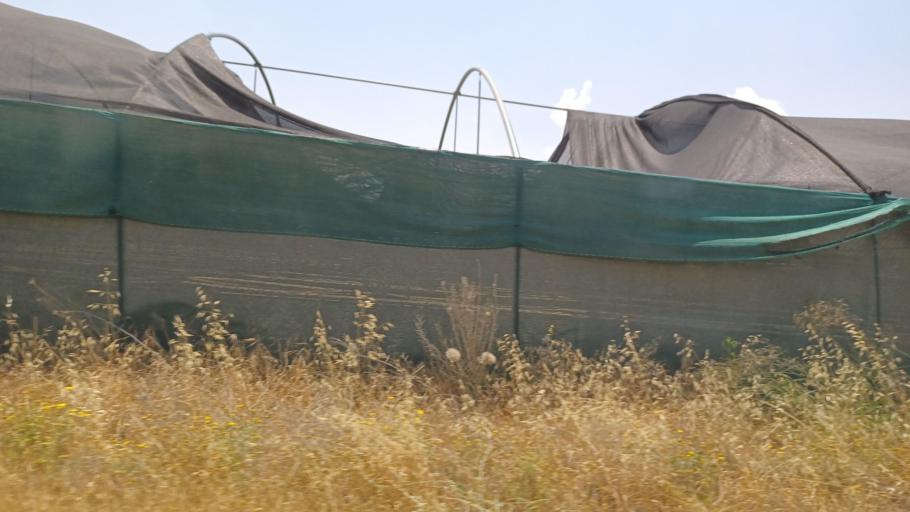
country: CY
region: Larnaka
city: Troulloi
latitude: 35.0351
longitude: 33.6001
